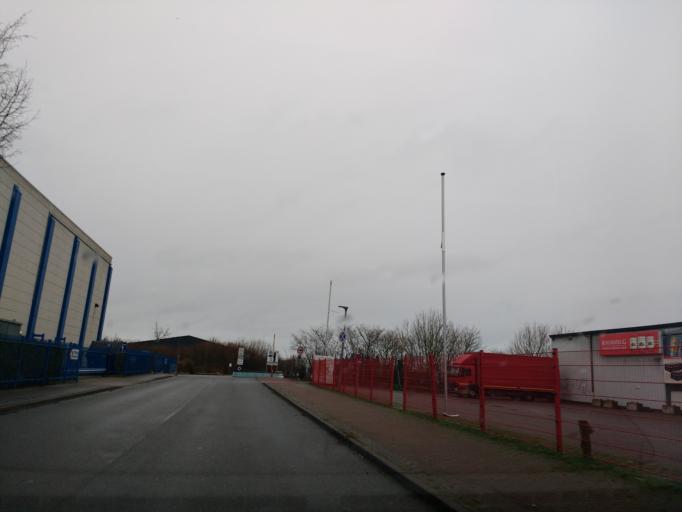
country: DE
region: Schleswig-Holstein
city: Fehmarn
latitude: 54.4456
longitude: 11.1812
